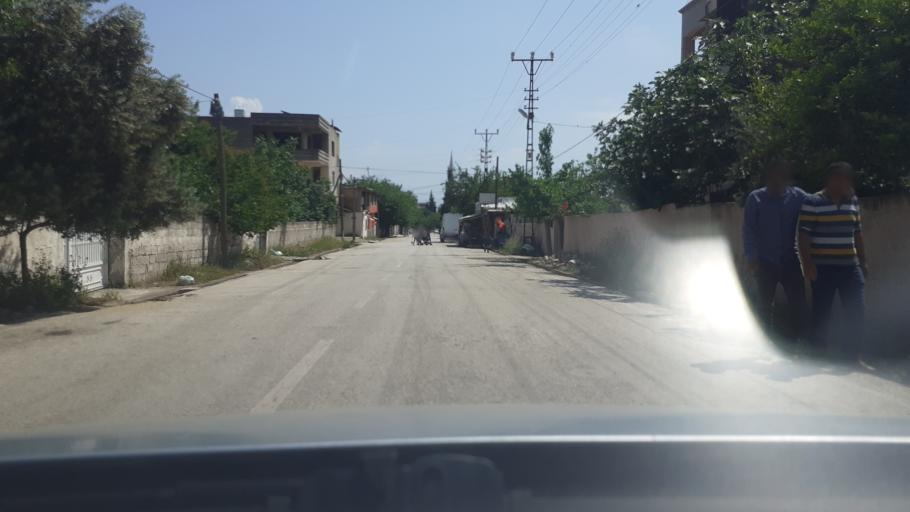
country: TR
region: Hatay
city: Kirikhan
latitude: 36.4894
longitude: 36.3540
